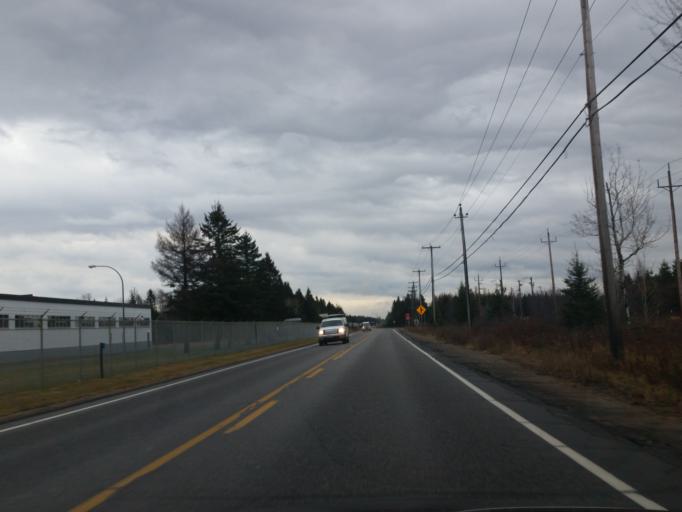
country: CA
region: Quebec
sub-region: Capitale-Nationale
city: Shannon
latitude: 46.8822
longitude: -71.4773
